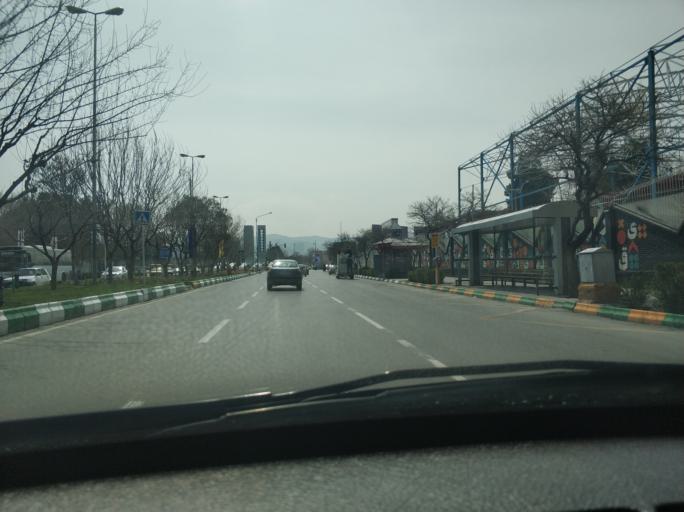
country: IR
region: Razavi Khorasan
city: Mashhad
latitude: 36.3016
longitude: 59.5640
